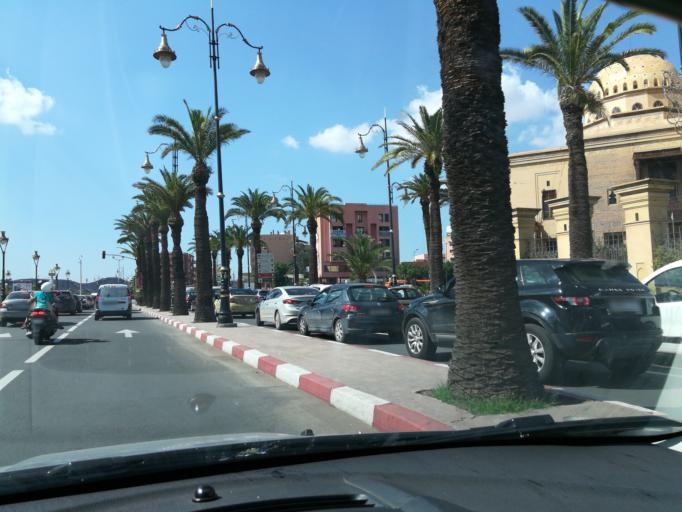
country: MA
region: Marrakech-Tensift-Al Haouz
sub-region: Marrakech
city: Marrakesh
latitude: 31.6293
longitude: -8.0154
